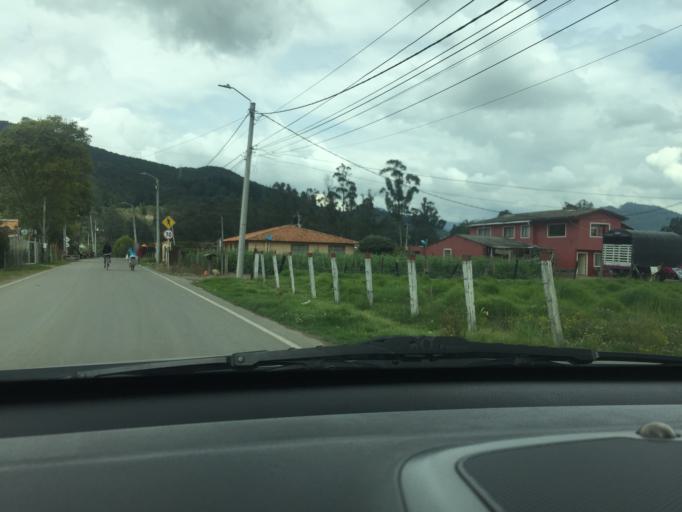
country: CO
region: Cundinamarca
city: Chia
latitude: 4.8768
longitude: -74.0704
